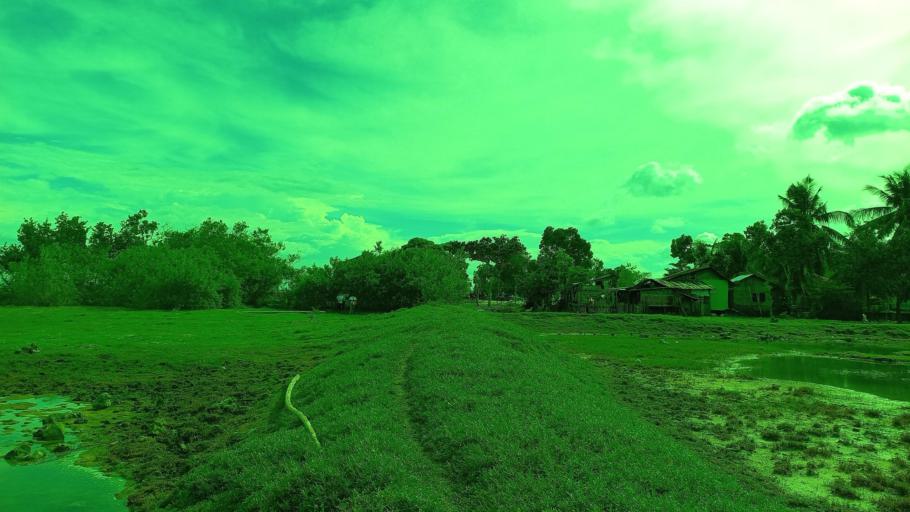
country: PH
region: Central Visayas
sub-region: Province of Siquijor
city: Lazi
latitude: 9.1252
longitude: 123.6483
